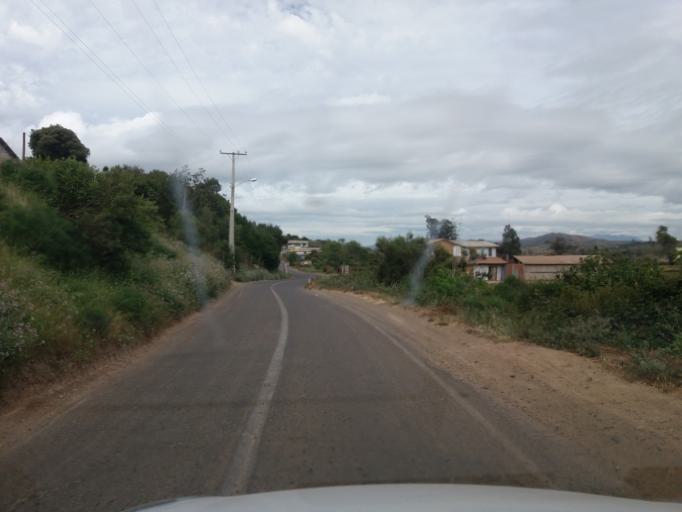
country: CL
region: Valparaiso
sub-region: Provincia de Marga Marga
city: Villa Alemana
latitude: -32.9163
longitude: -71.3900
